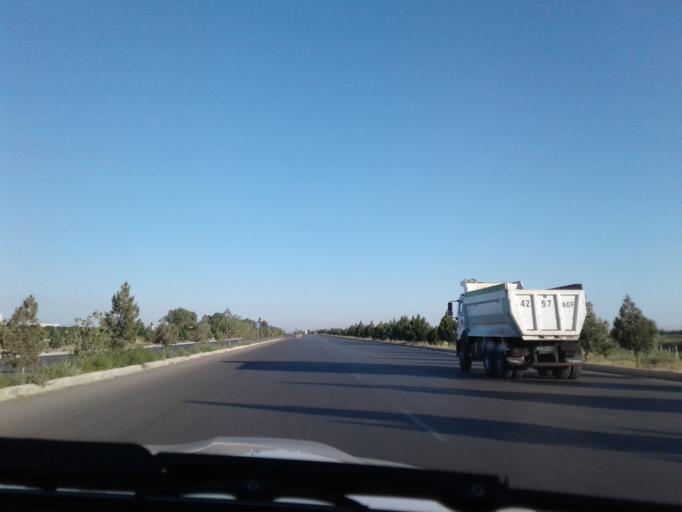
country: TM
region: Ahal
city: Abadan
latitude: 38.0655
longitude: 58.2548
